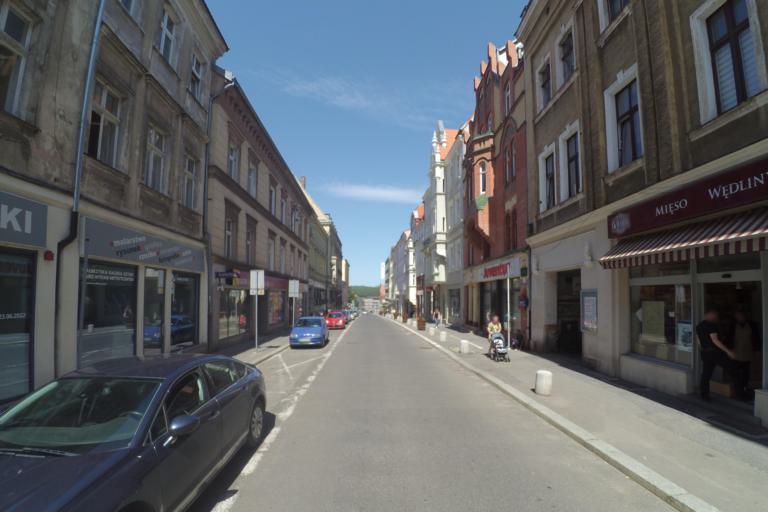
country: PL
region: Lower Silesian Voivodeship
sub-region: Powiat walbrzyski
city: Walbrzych
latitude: 50.7678
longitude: 16.2808
